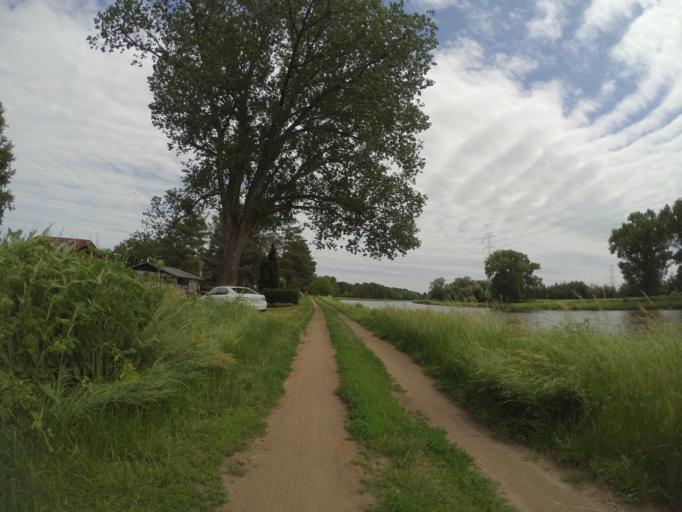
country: CZ
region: Central Bohemia
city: Celakovice
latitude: 50.1727
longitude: 14.7758
